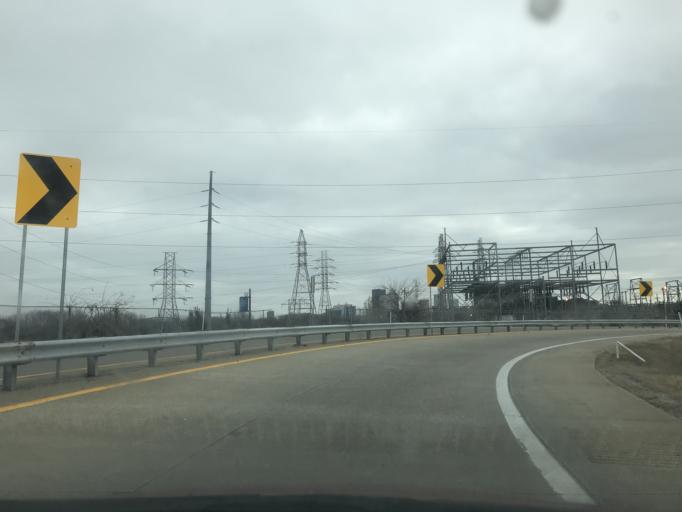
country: US
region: Kentucky
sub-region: Jefferson County
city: Louisville
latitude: 38.2719
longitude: -85.7819
